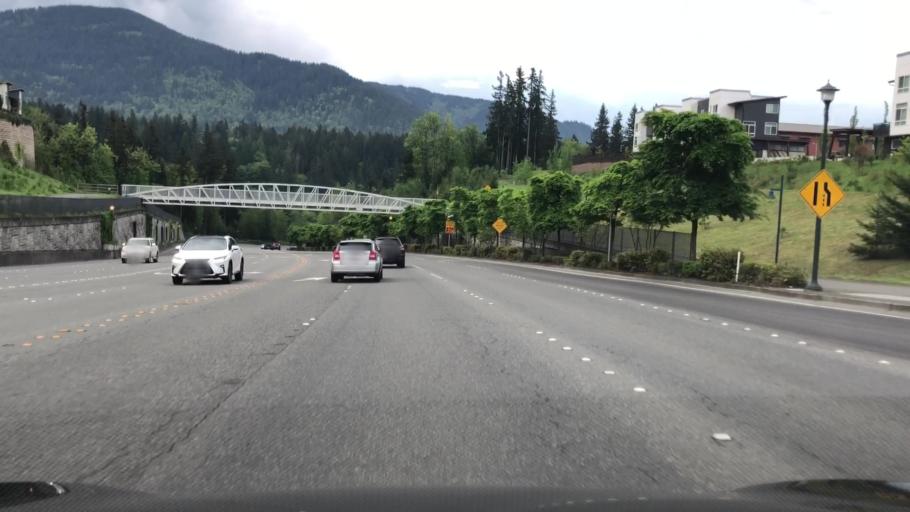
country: US
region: Washington
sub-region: King County
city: Issaquah
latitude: 47.5389
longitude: -122.0195
